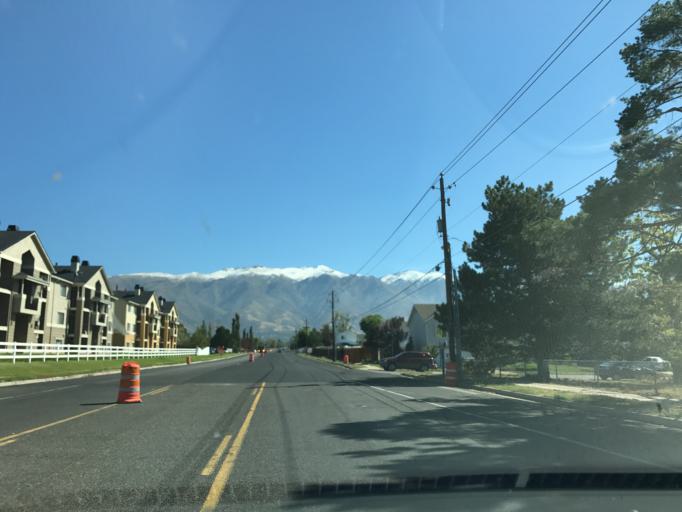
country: US
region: Utah
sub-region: Davis County
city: Hill Air Force Bace
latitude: 41.0892
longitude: -111.9718
